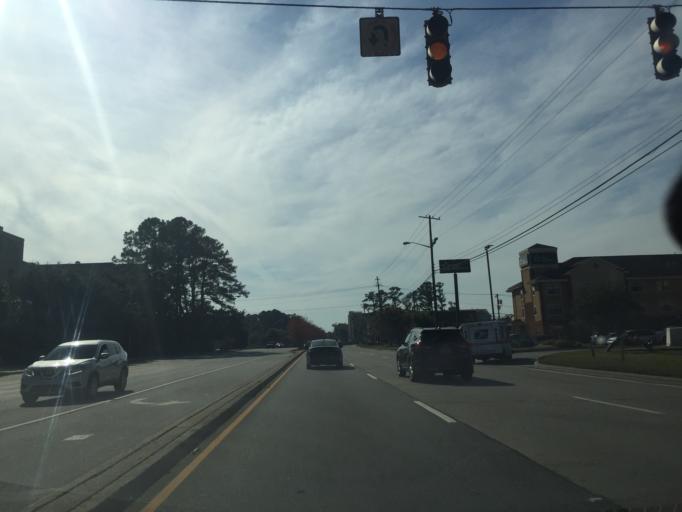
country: US
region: Georgia
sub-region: Chatham County
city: Savannah
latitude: 32.0262
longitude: -81.1090
